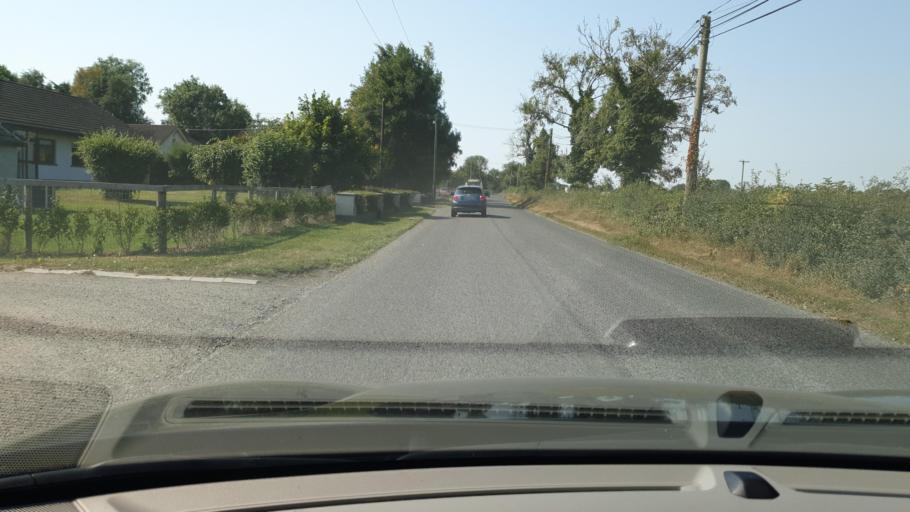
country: IE
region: Leinster
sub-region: An Mhi
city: Trim
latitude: 53.5694
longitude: -6.8209
